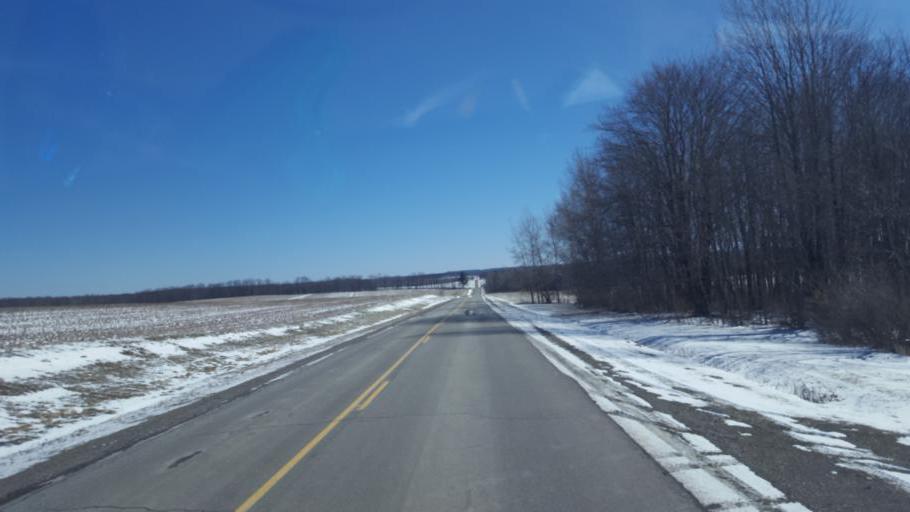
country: US
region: New York
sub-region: Allegany County
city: Andover
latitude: 42.0608
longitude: -77.8058
